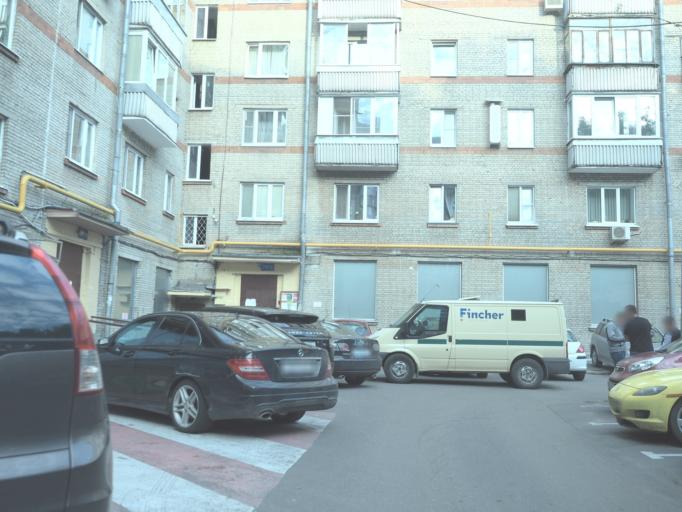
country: RU
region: Moscow
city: Novyye Cheremushki
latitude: 55.7072
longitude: 37.5777
